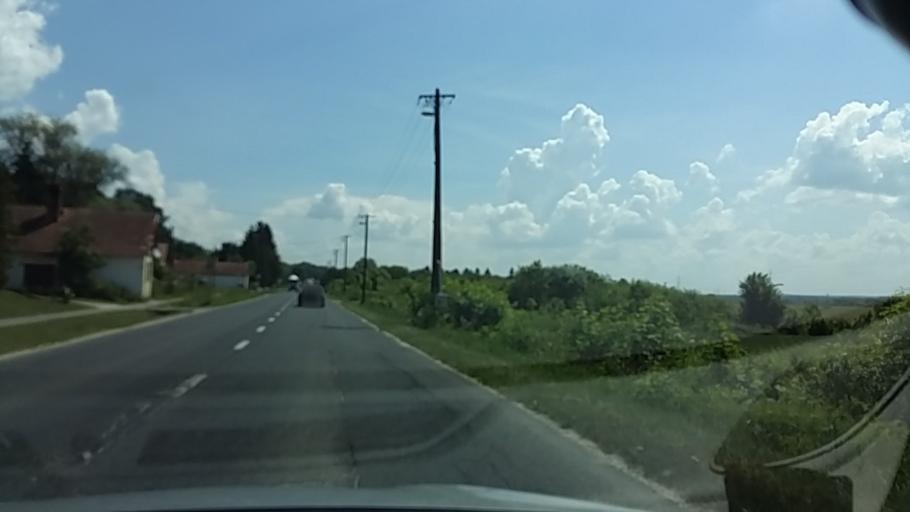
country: AT
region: Burgenland
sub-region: Politischer Bezirk Gussing
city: Inzenhof
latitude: 46.9770
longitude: 16.3573
